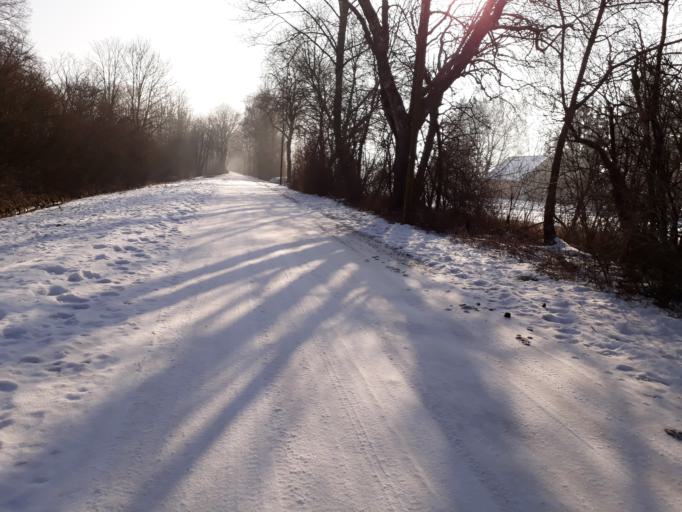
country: DE
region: Bavaria
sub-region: Upper Bavaria
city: Ismaning
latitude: 48.2012
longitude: 11.6791
